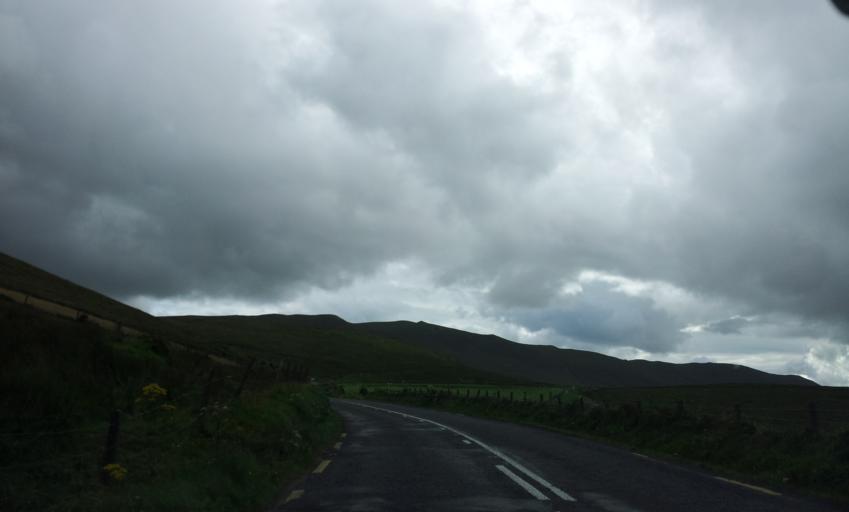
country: IE
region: Munster
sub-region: Ciarrai
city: Killorglin
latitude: 52.2059
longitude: -9.9305
